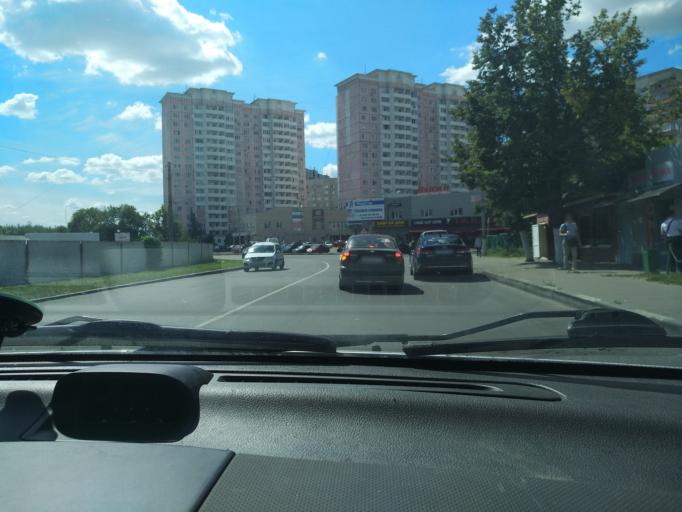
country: RU
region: Moskovskaya
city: Zhukovskiy
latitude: 55.5962
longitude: 38.0949
